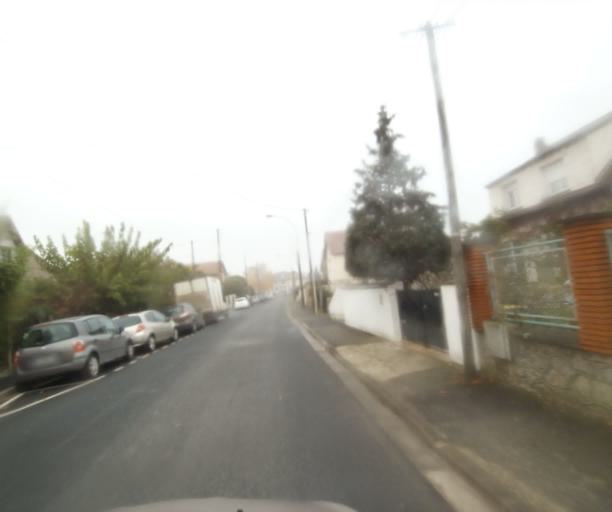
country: FR
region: Ile-de-France
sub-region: Departement de Seine-Saint-Denis
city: Vaujours
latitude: 48.9376
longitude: 2.5721
